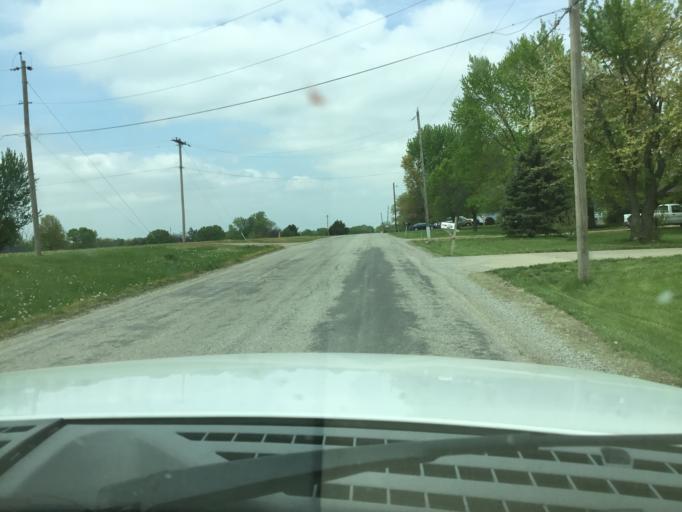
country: US
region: Kansas
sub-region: Shawnee County
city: Topeka
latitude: 38.9911
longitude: -95.5864
